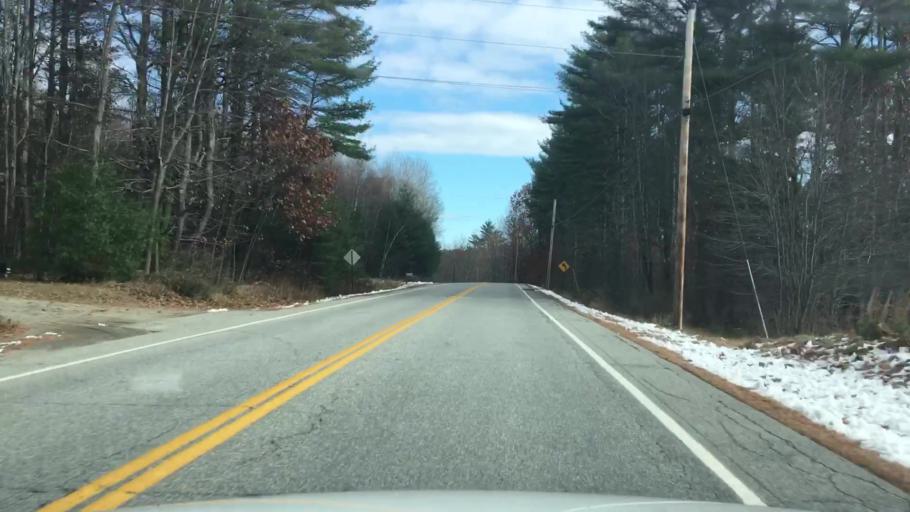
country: US
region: Maine
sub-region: Kennebec County
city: Wayne
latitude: 44.3508
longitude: -70.0987
